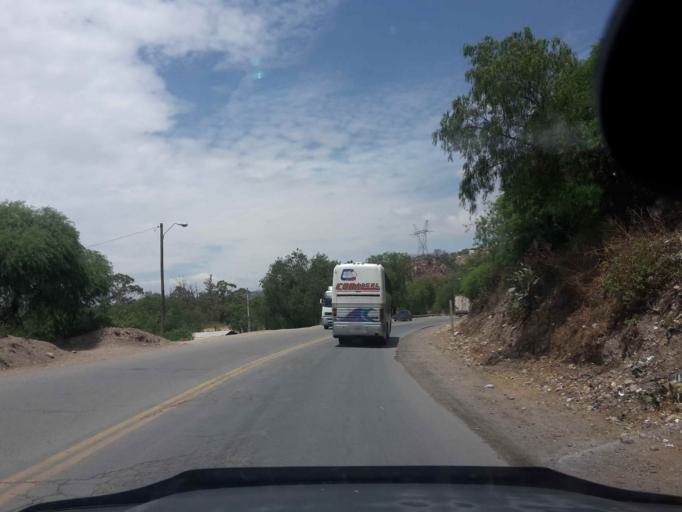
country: BO
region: Cochabamba
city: Sipe Sipe
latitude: -17.5573
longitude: -66.3417
